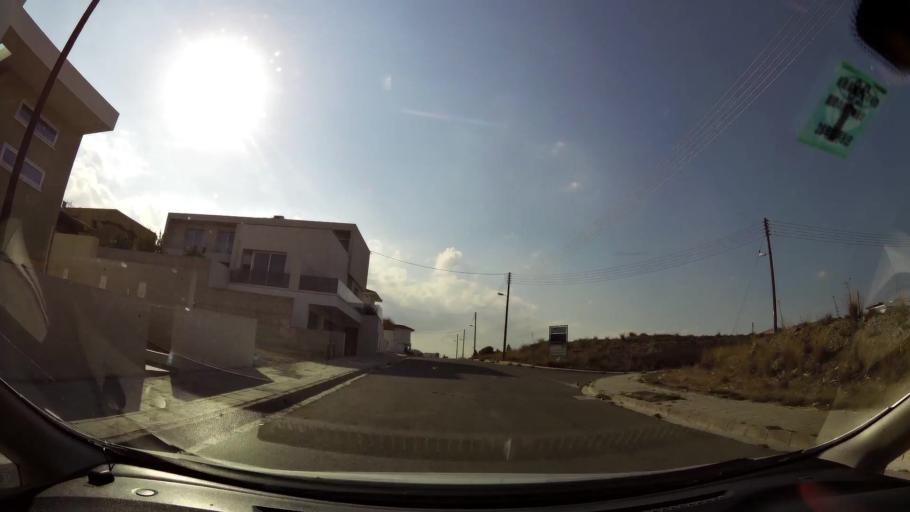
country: CY
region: Lefkosia
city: Kato Deftera
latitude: 35.1400
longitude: 33.2990
